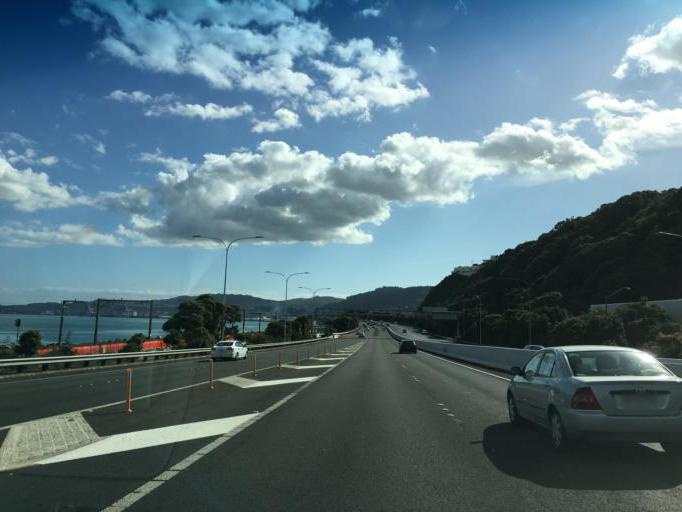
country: NZ
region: Wellington
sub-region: Wellington City
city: Wellington
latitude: -41.2492
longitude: 174.8116
